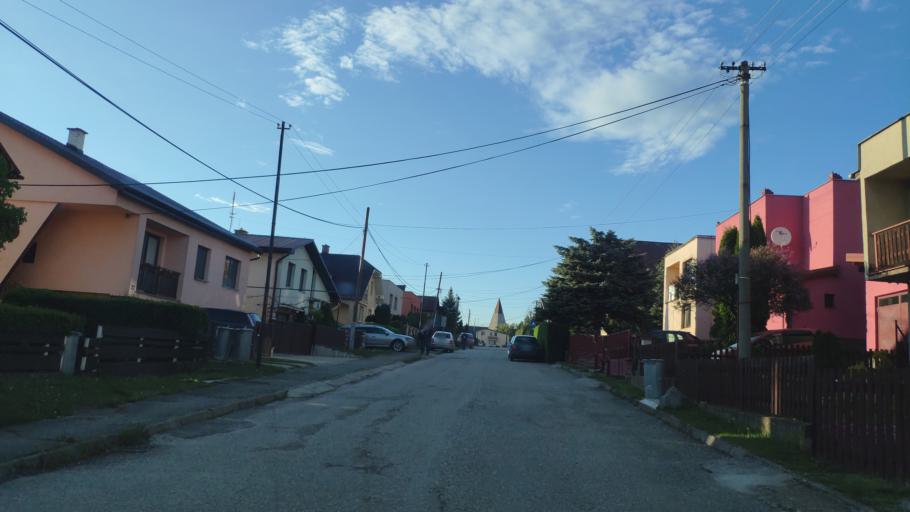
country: SK
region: Kosicky
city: Kosice
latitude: 48.7503
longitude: 21.3473
